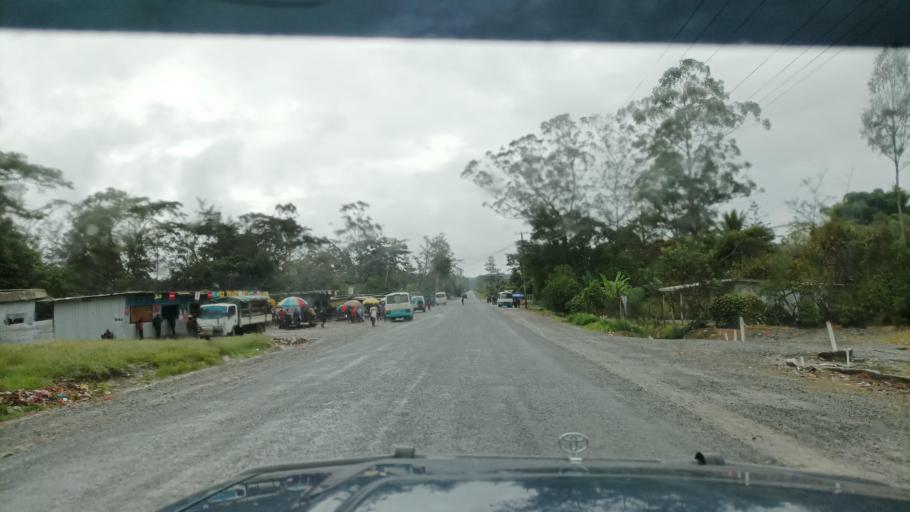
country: PG
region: Western Highlands
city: Rauna
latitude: -5.8243
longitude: 144.3862
